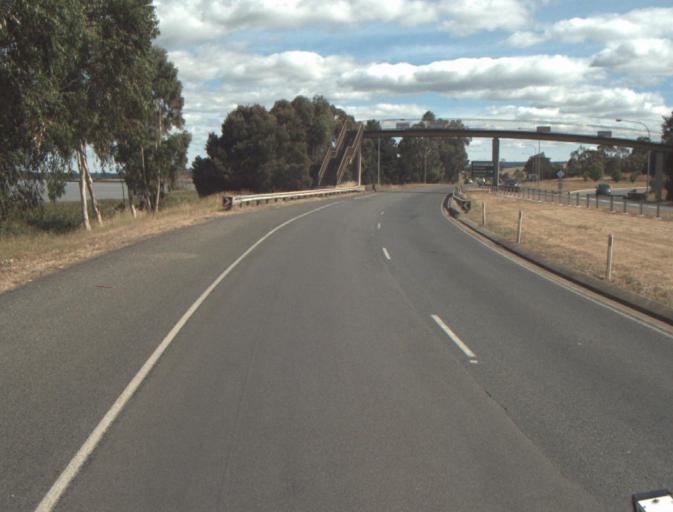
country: AU
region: Tasmania
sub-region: Launceston
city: Newnham
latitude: -41.4009
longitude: 147.1167
